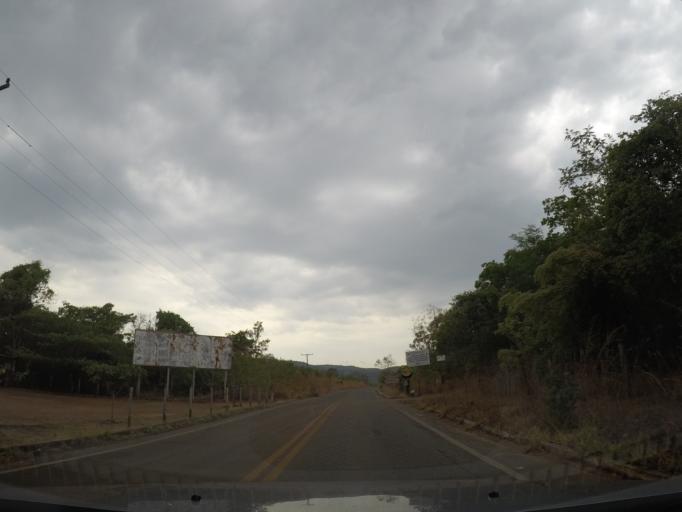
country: BR
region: Goias
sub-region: Pirenopolis
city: Pirenopolis
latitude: -15.8480
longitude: -48.9262
